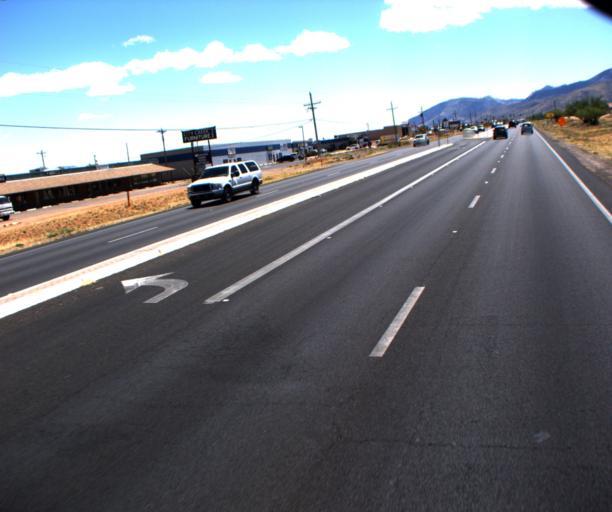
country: US
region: Arizona
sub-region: Cochise County
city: Sierra Vista Southeast
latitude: 31.5010
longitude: -110.2575
